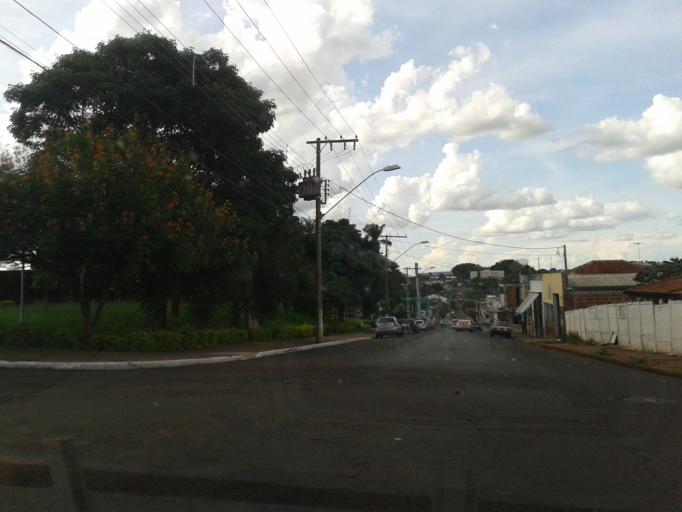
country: BR
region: Minas Gerais
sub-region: Ituiutaba
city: Ituiutaba
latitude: -18.9749
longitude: -49.4544
